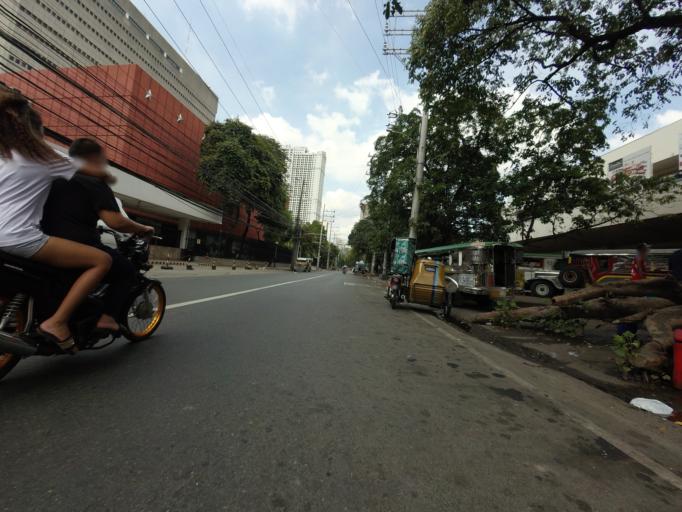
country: PH
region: Metro Manila
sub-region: City of Manila
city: Port Area
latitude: 14.5623
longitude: 120.9884
